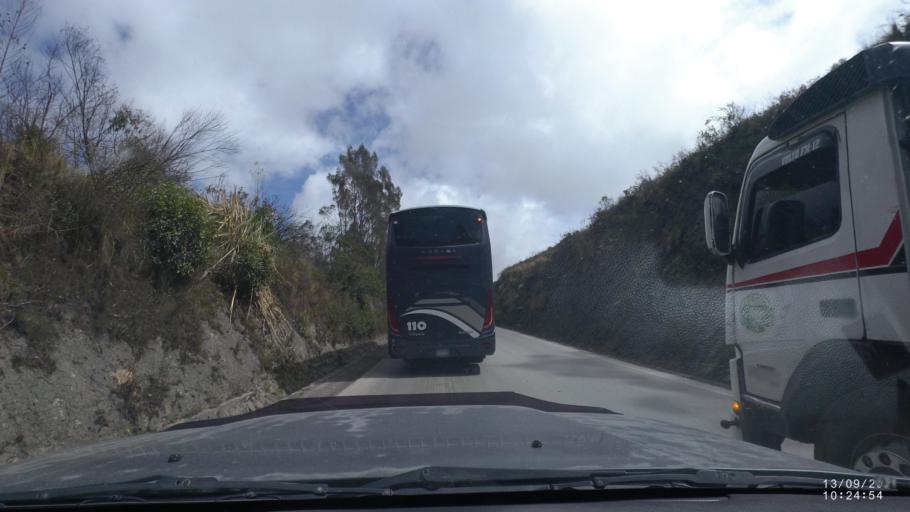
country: BO
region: Cochabamba
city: Colomi
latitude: -17.3152
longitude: -65.8616
